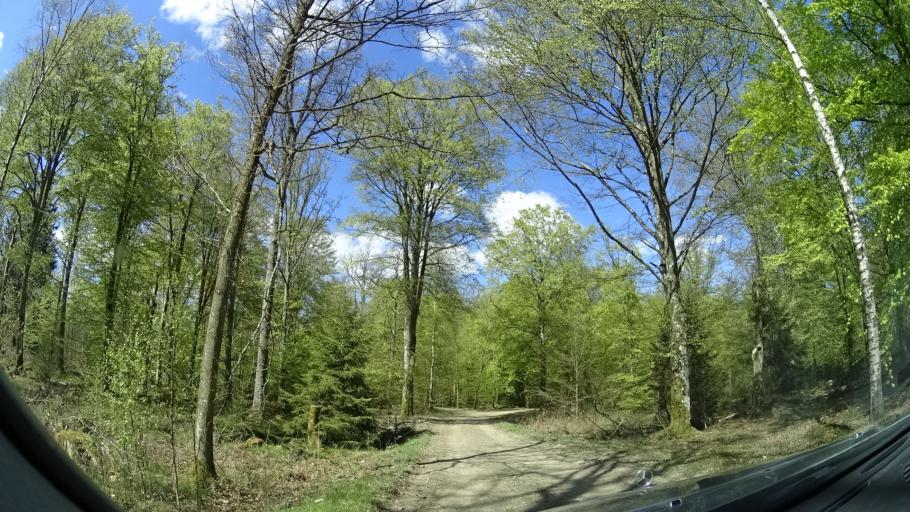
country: SE
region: Skane
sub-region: Hassleholms Kommun
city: Tormestorp
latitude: 56.0927
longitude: 13.6918
